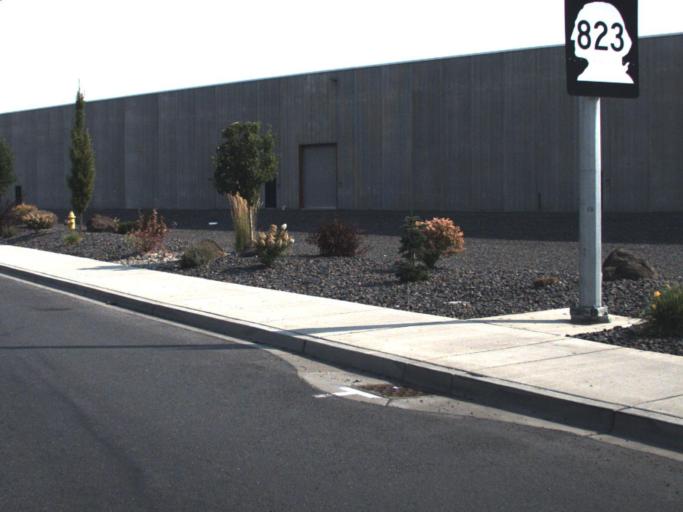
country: US
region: Washington
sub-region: Yakima County
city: Selah
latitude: 46.6494
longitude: -120.5287
